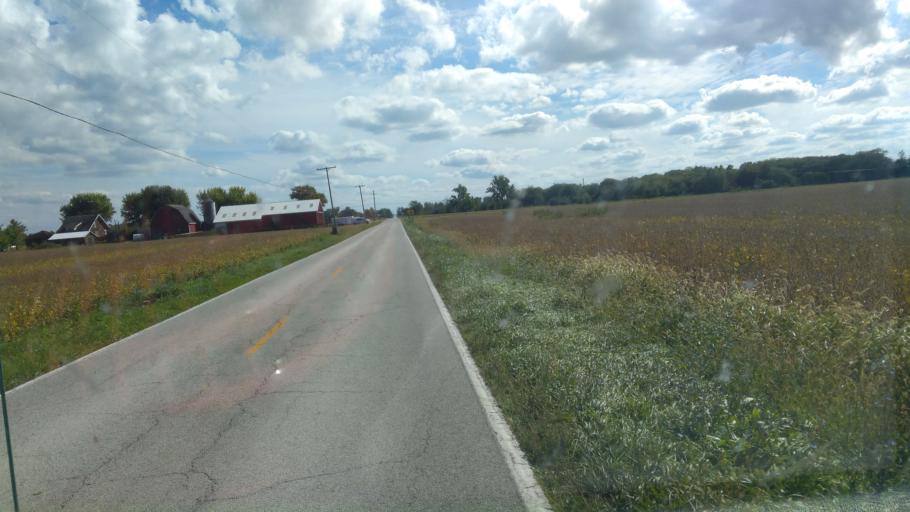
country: US
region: Ohio
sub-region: Sandusky County
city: Clyde
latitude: 41.3895
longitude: -82.9540
